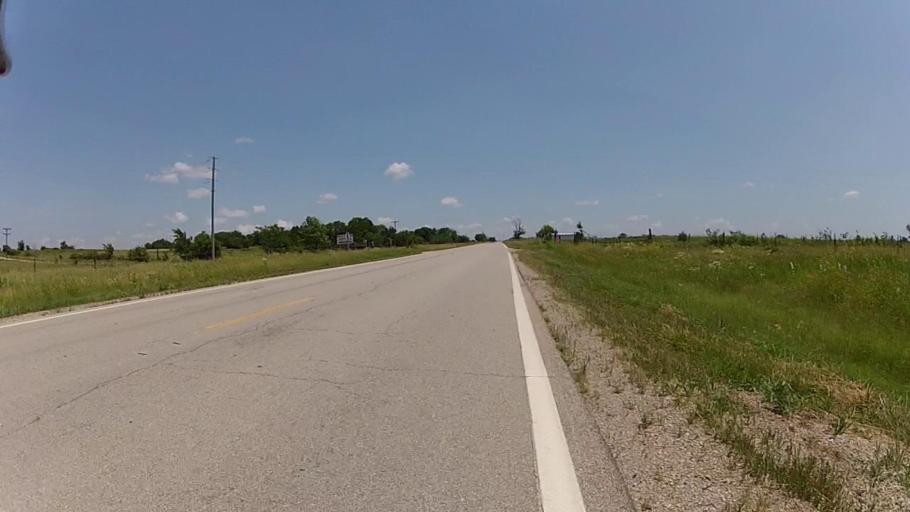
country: US
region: Kansas
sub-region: Montgomery County
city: Cherryvale
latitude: 37.1930
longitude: -95.4863
